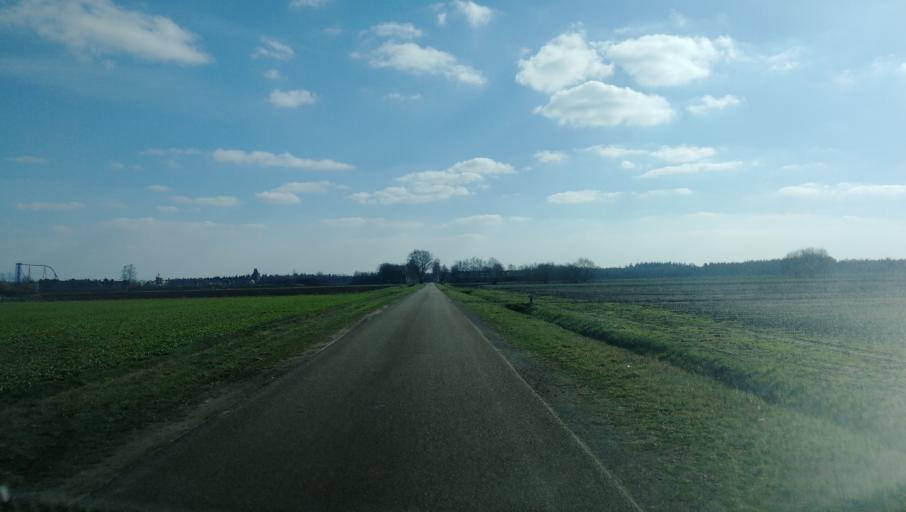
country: NL
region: Limburg
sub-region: Gemeente Peel en Maas
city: Maasbree
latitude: 51.4063
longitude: 5.9710
